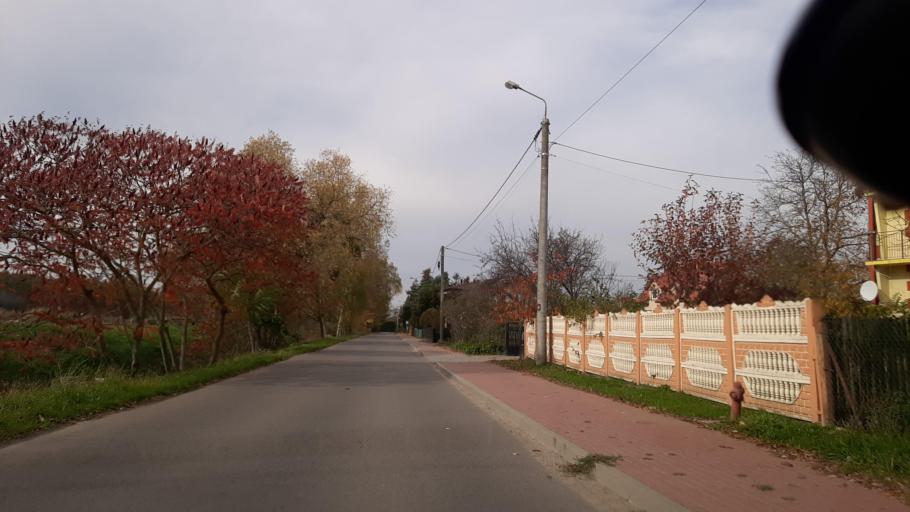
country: PL
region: Lublin Voivodeship
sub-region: Powiat pulawski
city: Markuszow
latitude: 51.3585
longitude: 22.2827
